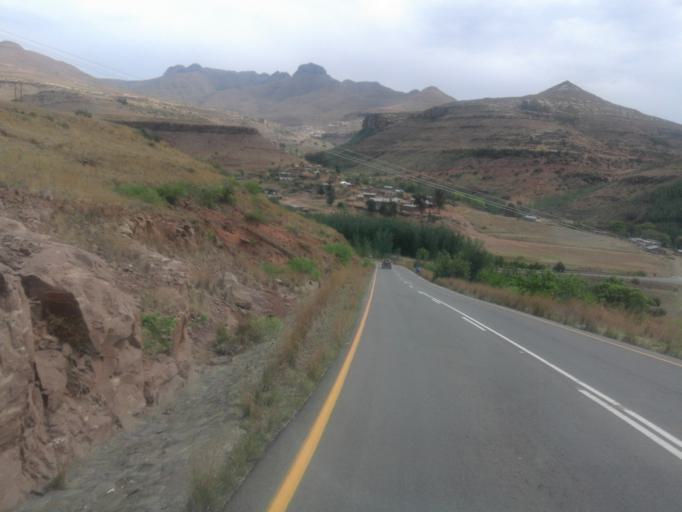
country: LS
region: Qacha's Nek
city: Qacha's Nek
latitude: -30.0784
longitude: 28.6245
